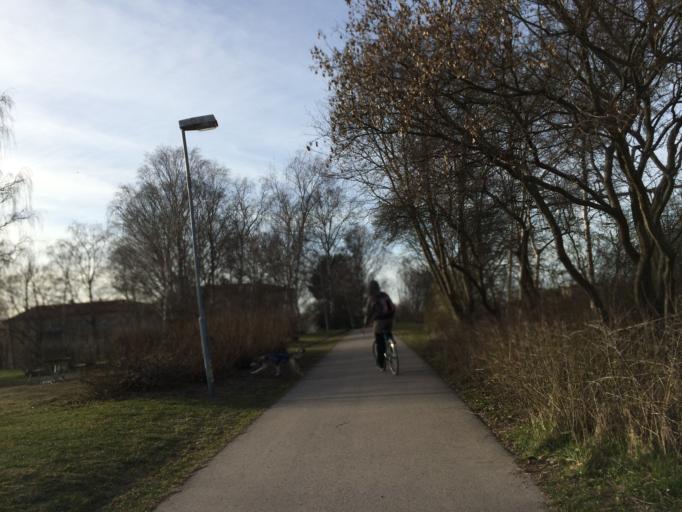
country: SE
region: Soedermanland
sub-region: Eskilstuna Kommun
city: Eskilstuna
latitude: 59.3741
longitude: 16.4918
